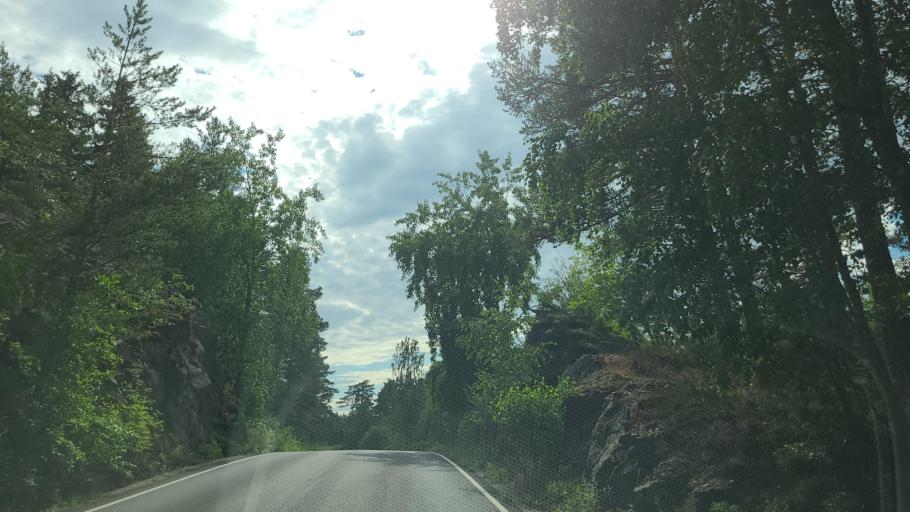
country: FI
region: Varsinais-Suomi
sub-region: Turku
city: Rymaettylae
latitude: 60.3308
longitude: 21.9744
